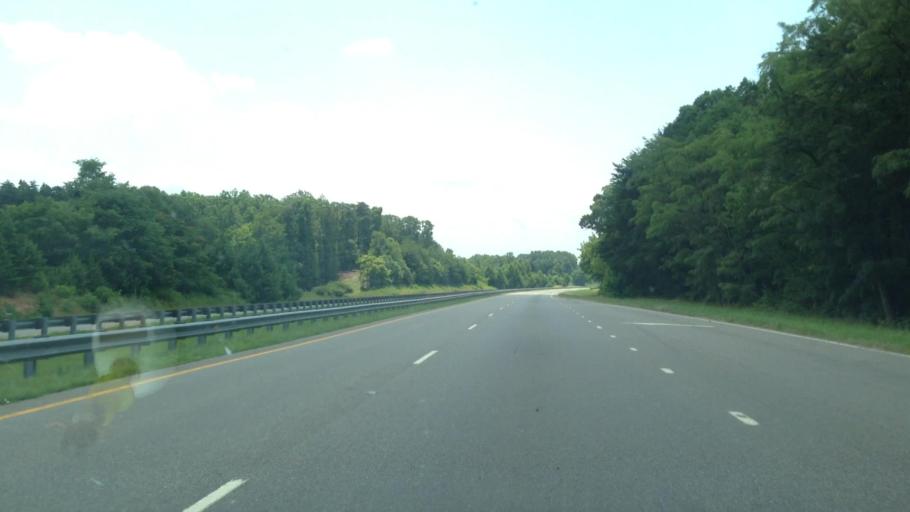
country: US
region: North Carolina
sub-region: Rockingham County
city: Stoneville
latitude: 36.4988
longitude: -79.9224
